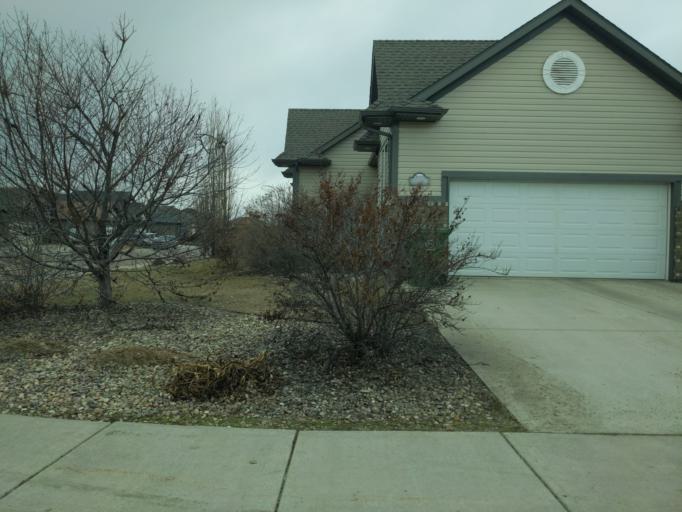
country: CA
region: Saskatchewan
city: Lloydminster
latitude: 53.2640
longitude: -110.0423
